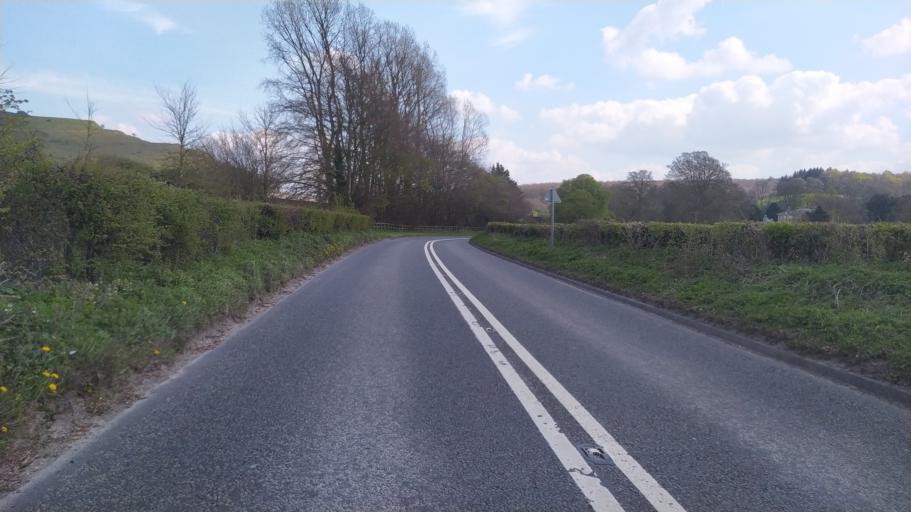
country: GB
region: England
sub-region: Wiltshire
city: Corsley
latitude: 51.2047
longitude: -2.2446
